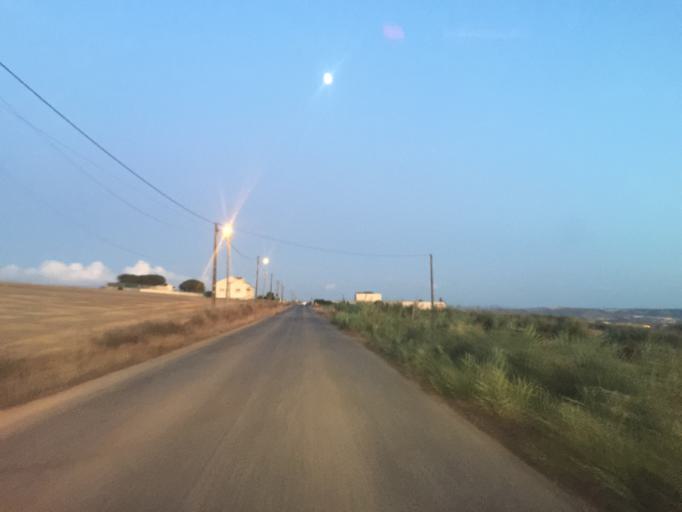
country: PT
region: Leiria
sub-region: Peniche
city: Atouguia da Baleia
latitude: 39.2910
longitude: -9.3081
